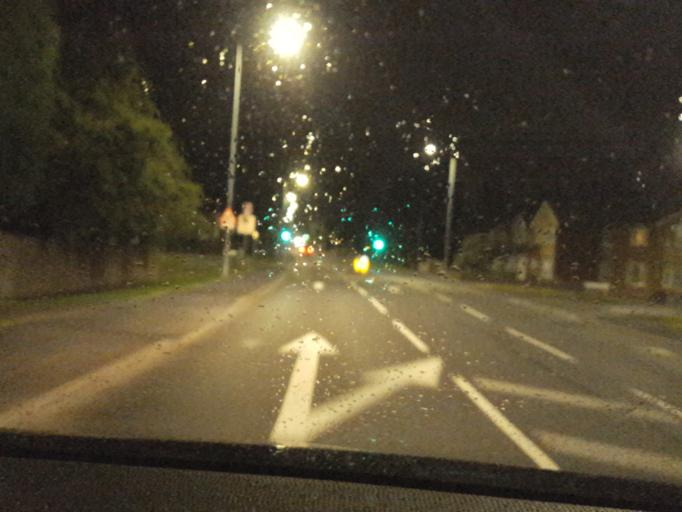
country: GB
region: England
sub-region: Leicestershire
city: Loughborough
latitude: 52.7586
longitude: -1.2316
